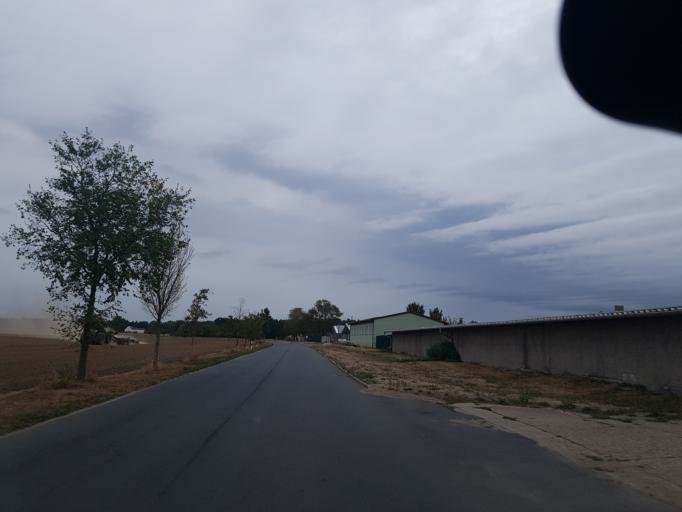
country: DE
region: Saxony-Anhalt
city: Prettin
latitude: 51.7050
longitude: 12.9012
